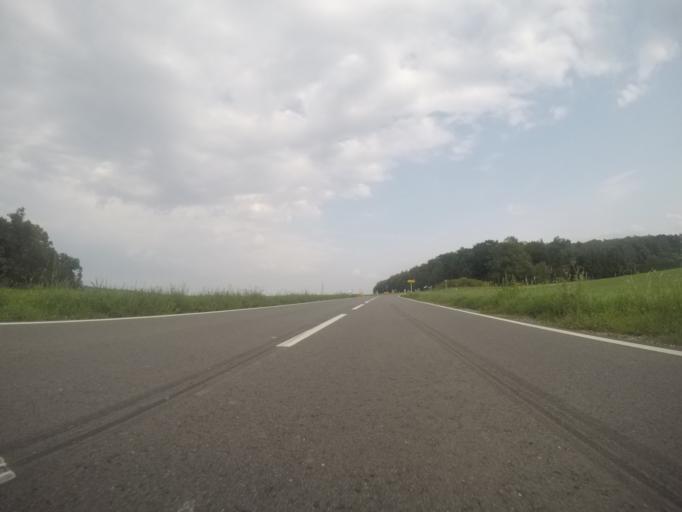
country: DE
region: Baden-Wuerttemberg
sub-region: Regierungsbezirk Stuttgart
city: Eberdingen
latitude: 48.8648
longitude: 8.9879
